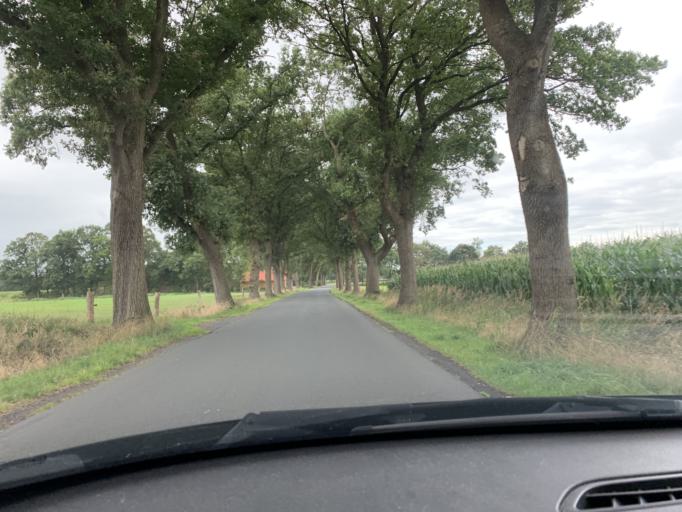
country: DE
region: Lower Saxony
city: Westerstede
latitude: 53.3112
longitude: 7.9074
